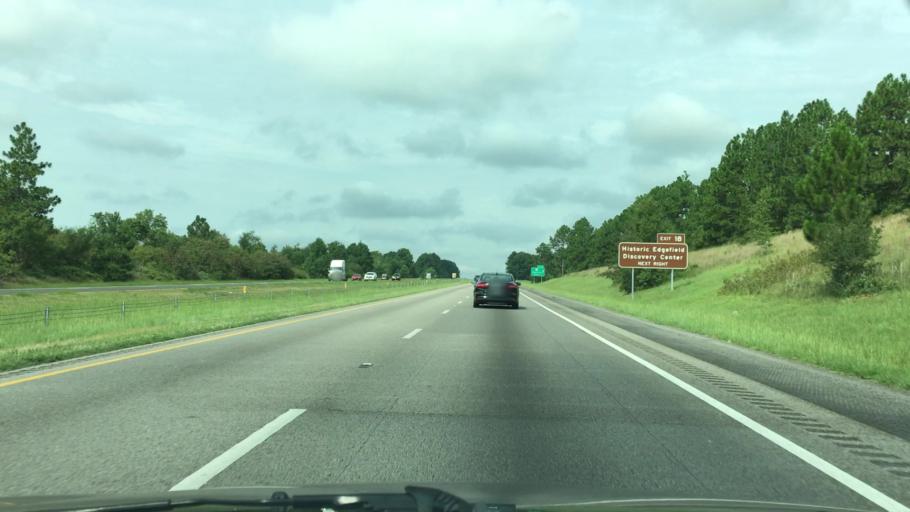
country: US
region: South Carolina
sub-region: Aiken County
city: Aiken
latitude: 33.6426
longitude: -81.7314
